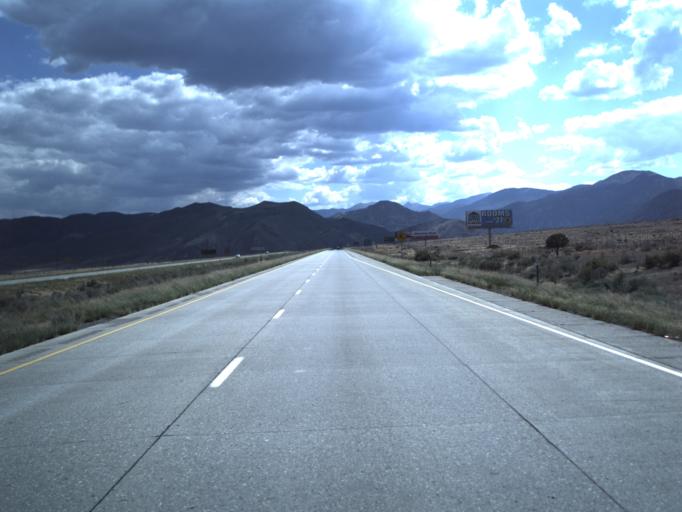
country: US
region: Utah
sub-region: Sevier County
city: Monroe
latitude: 38.6164
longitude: -112.2300
